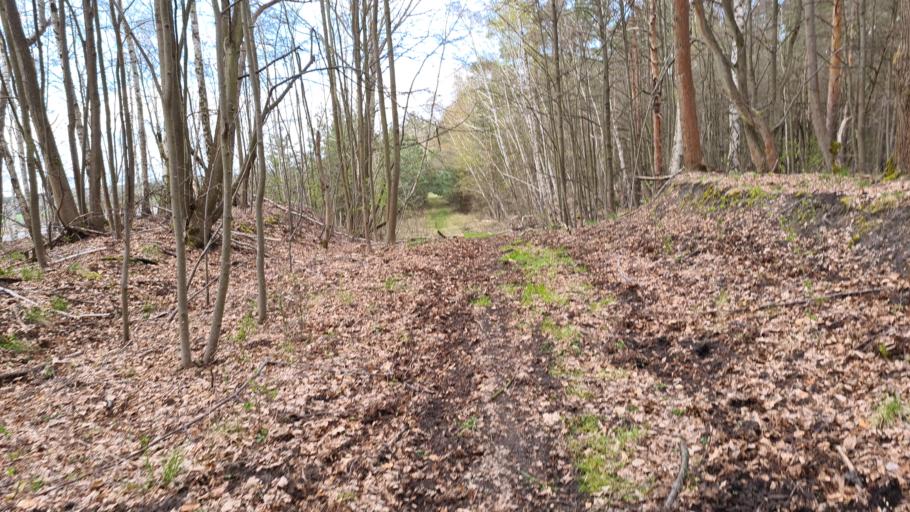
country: DE
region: Brandenburg
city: Trobitz
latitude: 51.5951
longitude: 13.4398
